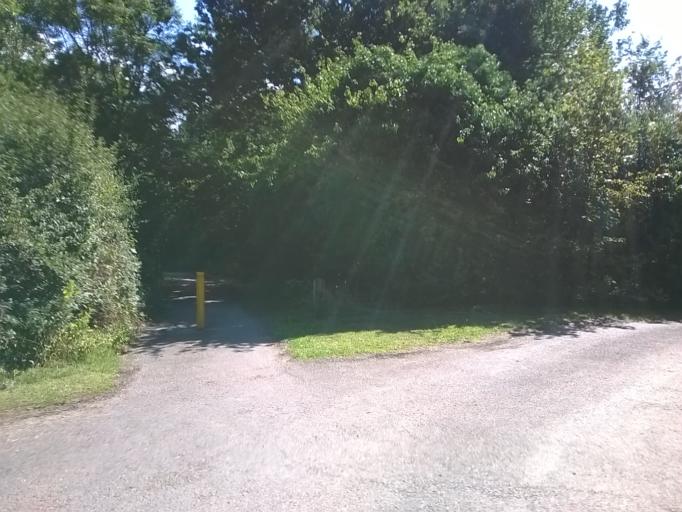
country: GB
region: England
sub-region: Milton Keynes
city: Milton Keynes
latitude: 52.0352
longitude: -0.7267
